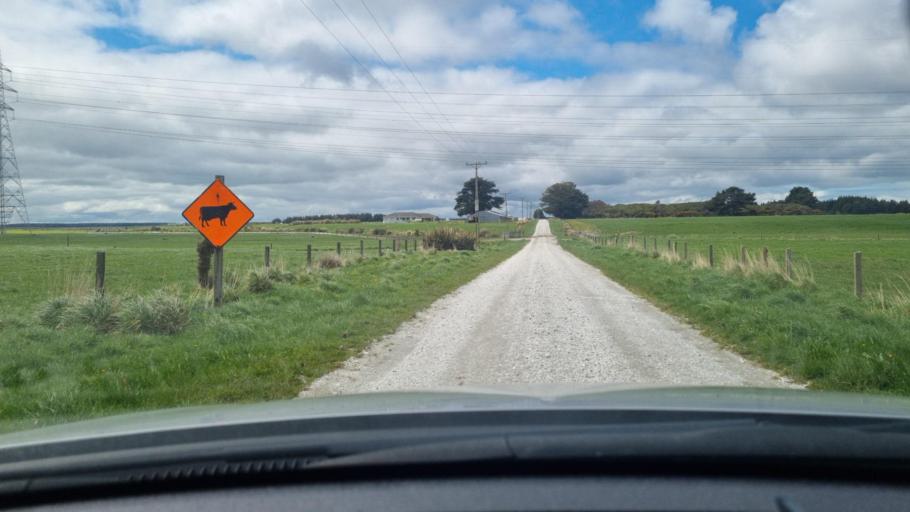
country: NZ
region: Southland
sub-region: Invercargill City
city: Invercargill
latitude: -46.5067
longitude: 168.4336
